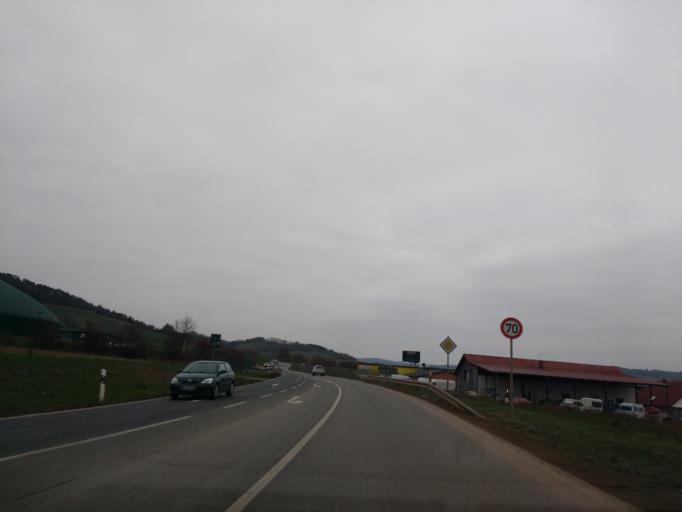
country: DE
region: Hesse
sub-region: Regierungsbezirk Kassel
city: Alheim
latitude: 51.0393
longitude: 9.6758
